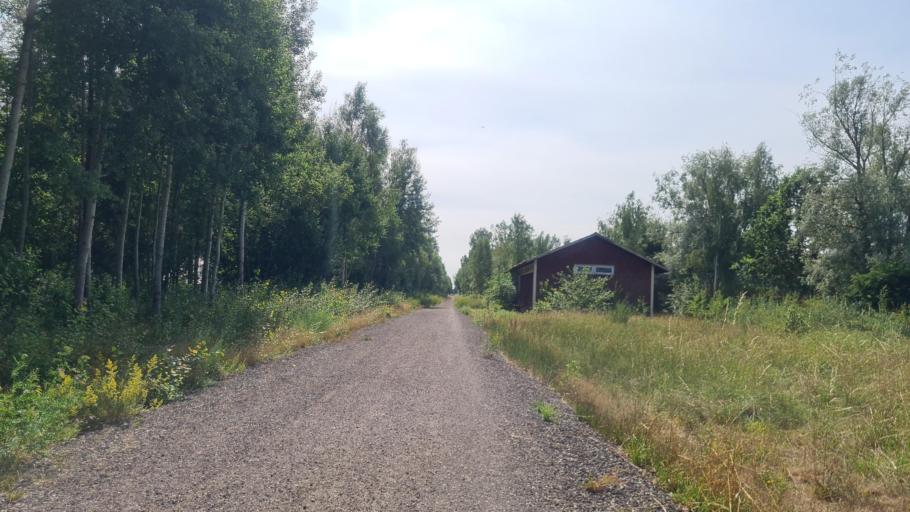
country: SE
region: Kronoberg
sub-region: Ljungby Kommun
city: Lagan
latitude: 56.9712
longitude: 13.9503
